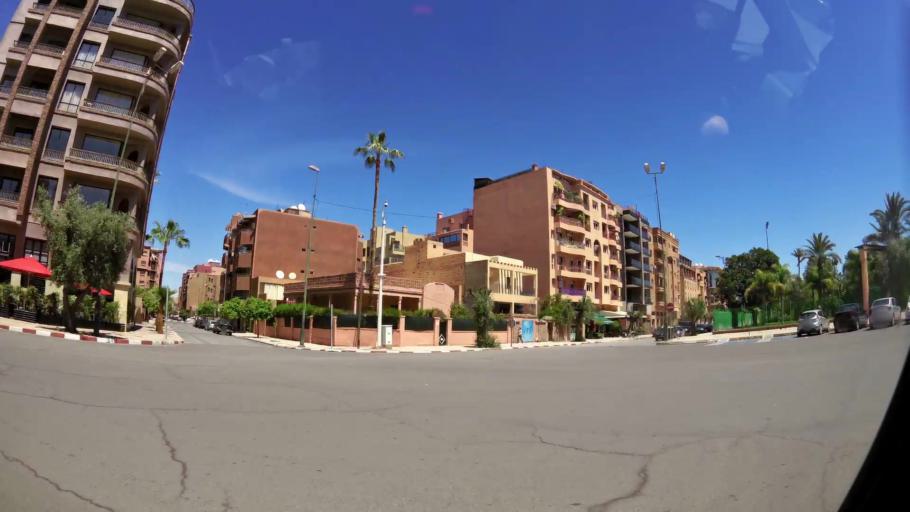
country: MA
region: Marrakech-Tensift-Al Haouz
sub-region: Marrakech
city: Marrakesh
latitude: 31.6299
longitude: -8.0125
